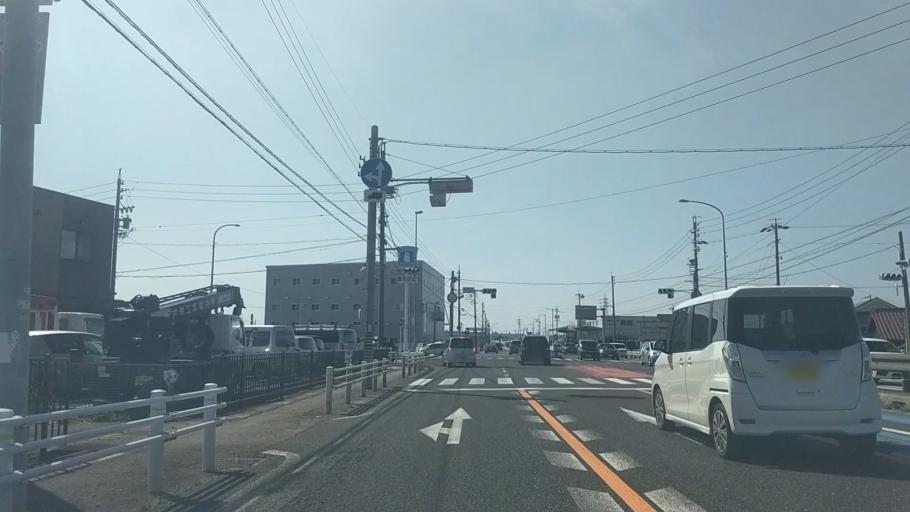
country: JP
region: Aichi
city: Anjo
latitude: 34.9766
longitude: 137.1143
